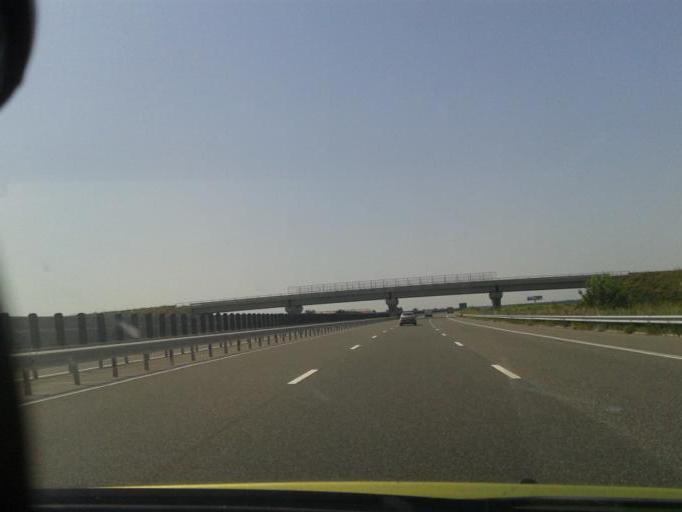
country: RO
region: Ilfov
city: Stefanestii de Jos
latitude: 44.5432
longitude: 26.1847
